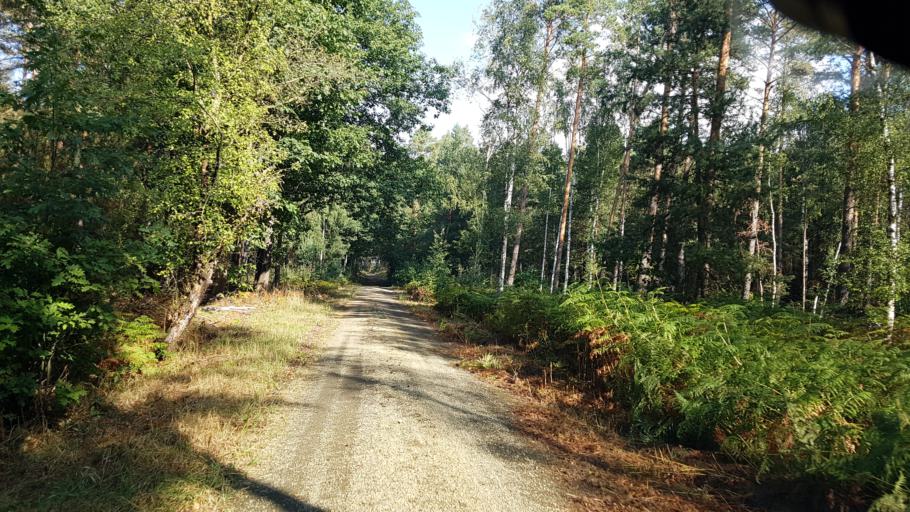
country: DE
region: Brandenburg
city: Plessa
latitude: 51.5167
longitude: 13.6401
